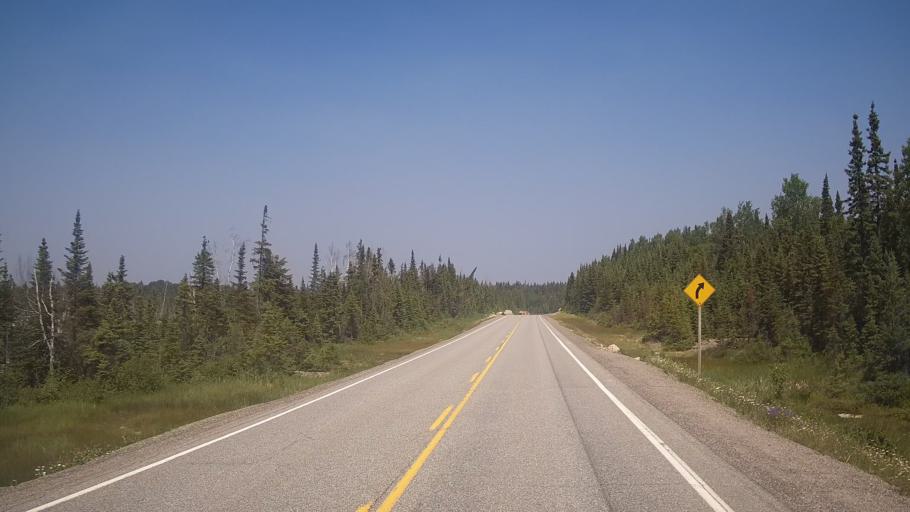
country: CA
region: Ontario
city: Timmins
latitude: 48.0723
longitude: -81.5926
